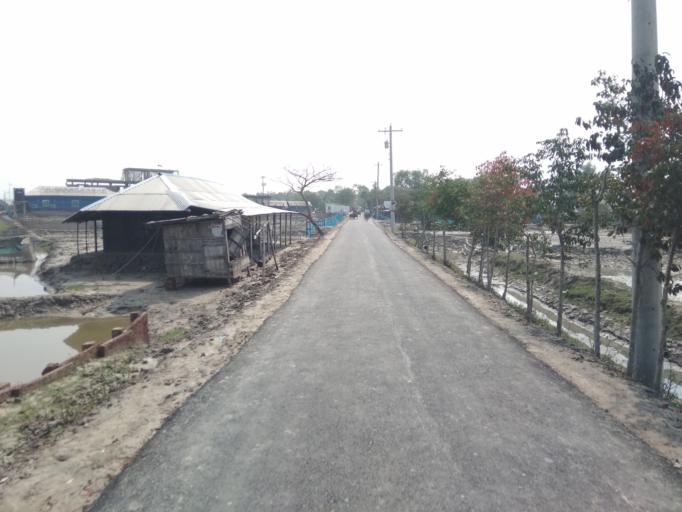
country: IN
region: West Bengal
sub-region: North 24 Parganas
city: Gosaba
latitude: 22.2619
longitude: 89.2234
